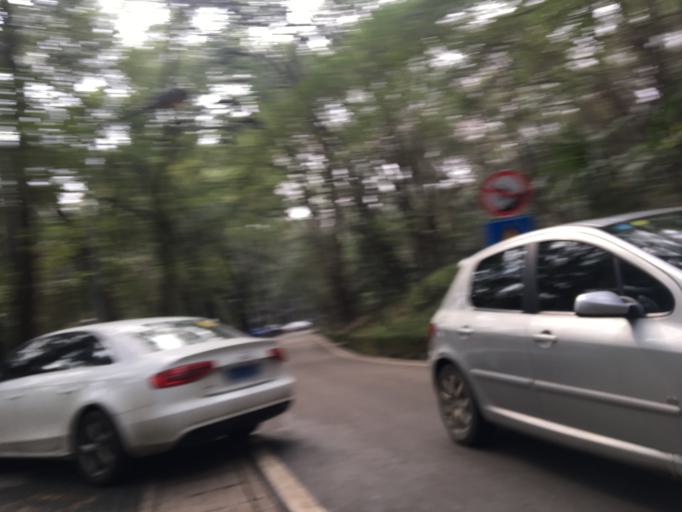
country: CN
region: Hubei
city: Guanshan
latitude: 30.5363
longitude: 114.3681
